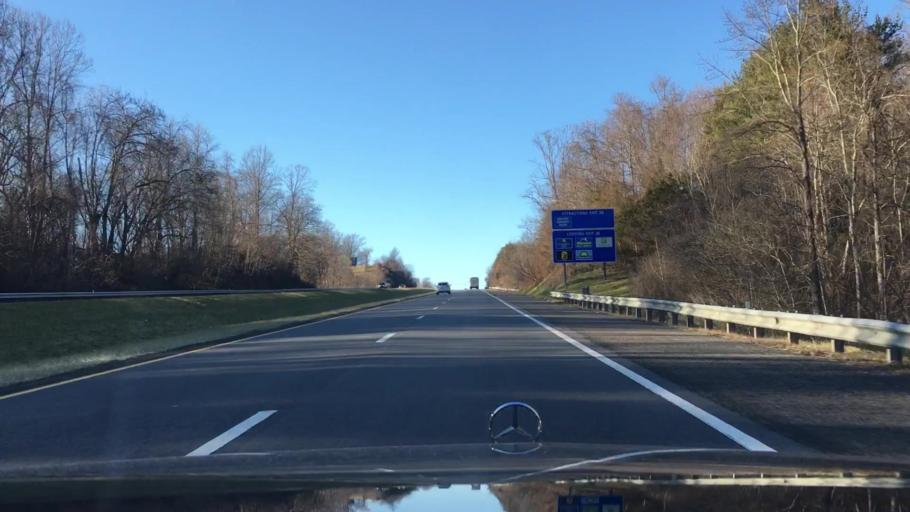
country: US
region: Virginia
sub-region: Montgomery County
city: Christiansburg
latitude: 37.1458
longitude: -80.3921
